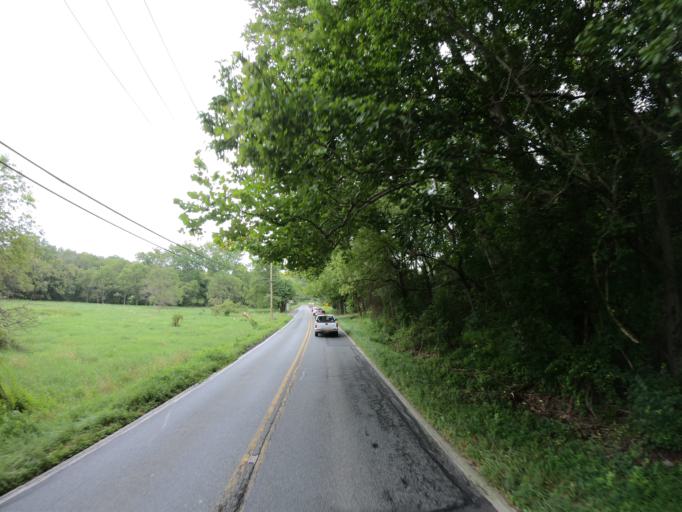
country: US
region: Maryland
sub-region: Montgomery County
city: Montgomery Village
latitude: 39.2026
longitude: -77.2051
